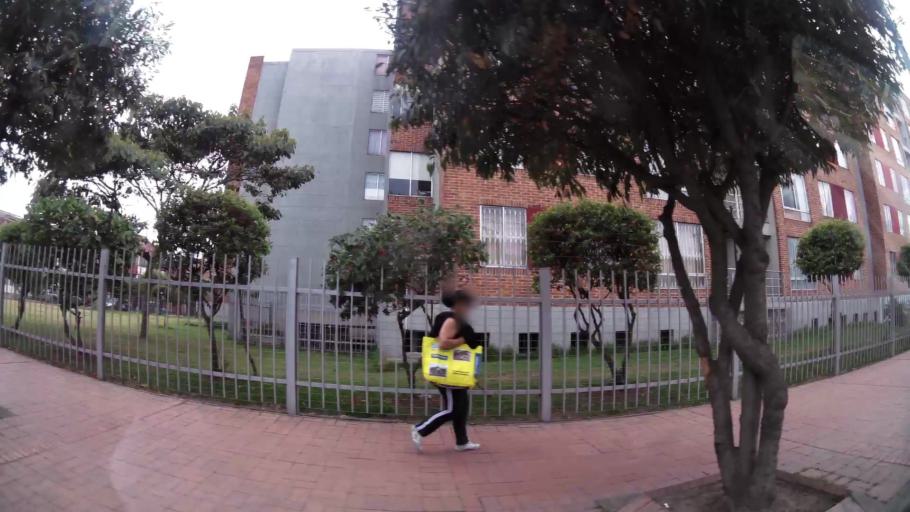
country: CO
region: Cundinamarca
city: Funza
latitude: 4.7149
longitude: -74.1278
